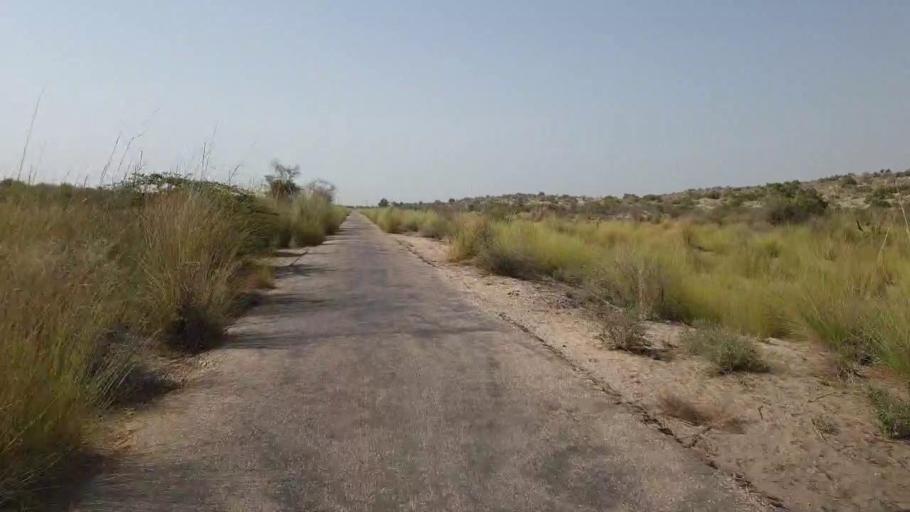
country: PK
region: Sindh
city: Jam Sahib
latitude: 26.5738
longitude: 68.9217
